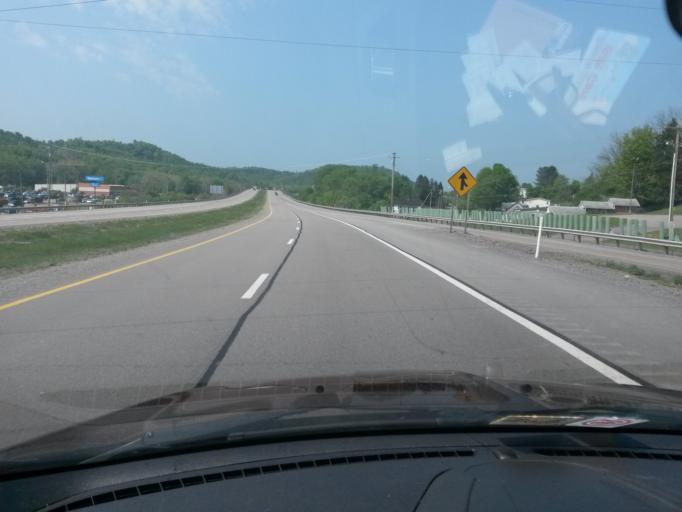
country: US
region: West Virginia
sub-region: Upshur County
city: Buckhannon
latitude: 39.0008
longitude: -80.2345
